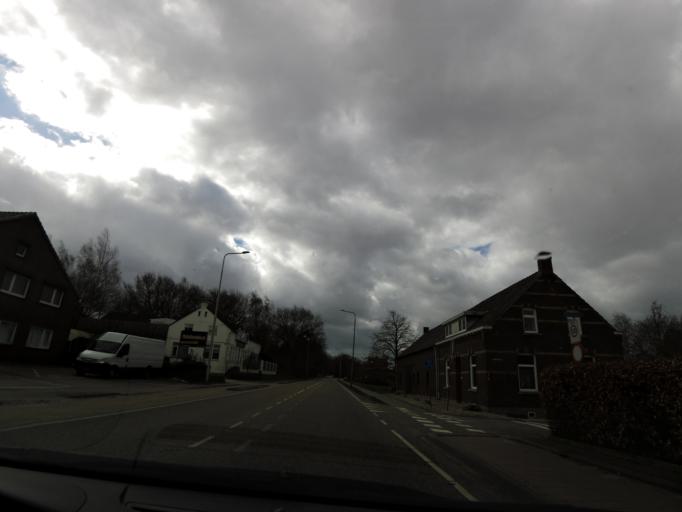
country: NL
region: Limburg
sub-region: Gemeente Beesel
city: Offenbeek
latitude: 51.3118
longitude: 6.1095
